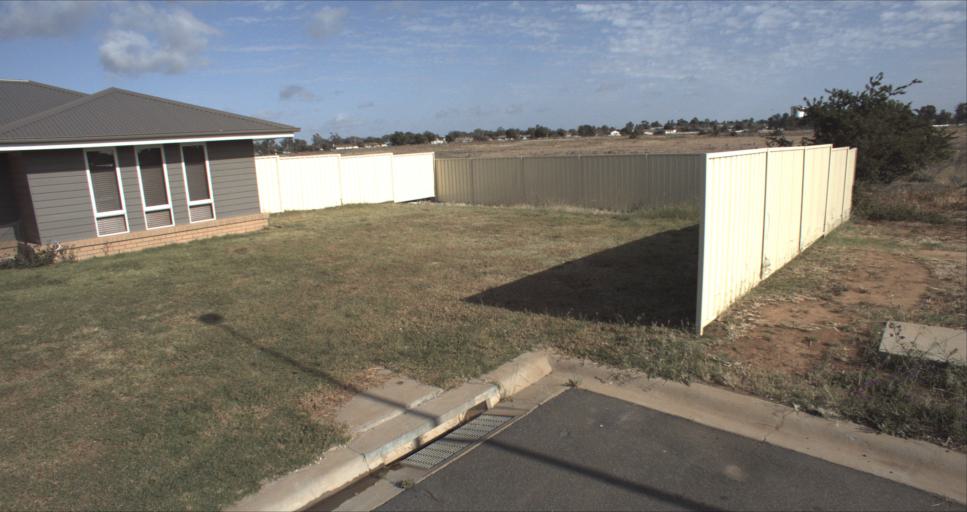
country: AU
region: New South Wales
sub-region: Leeton
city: Leeton
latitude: -34.5695
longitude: 146.3993
